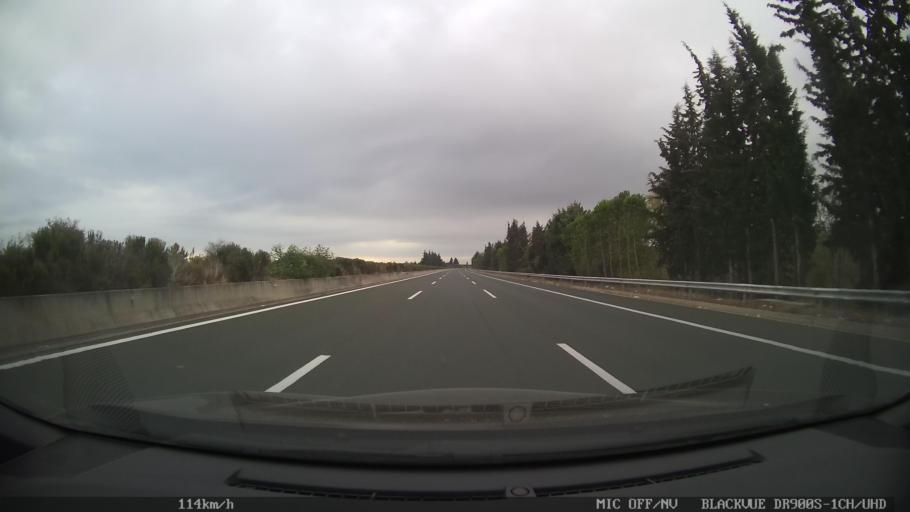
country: GR
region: Central Macedonia
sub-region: Nomos Pierias
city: Makrygialos
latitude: 40.4010
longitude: 22.5988
